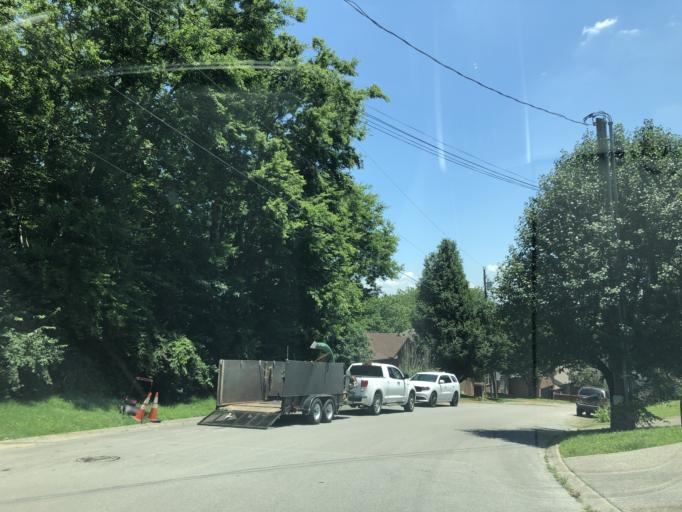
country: US
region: Tennessee
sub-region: Williamson County
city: Nolensville
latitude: 36.0368
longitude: -86.6812
